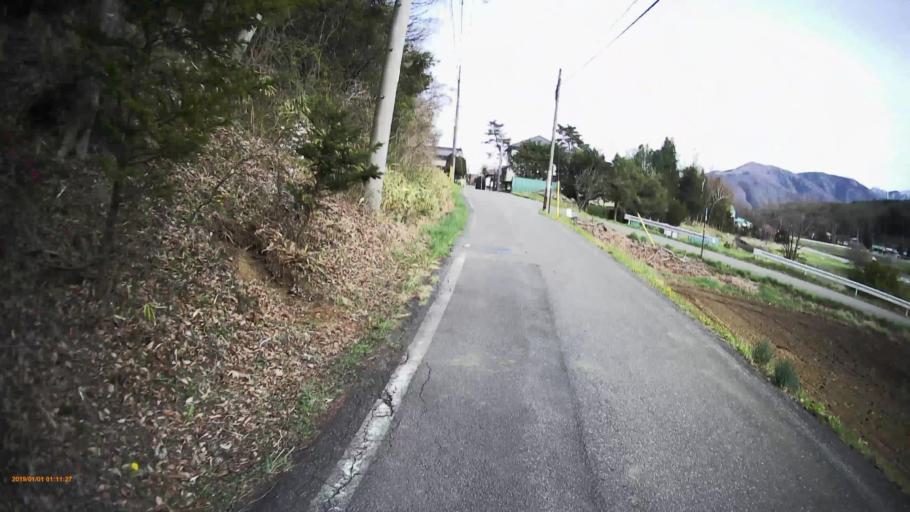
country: JP
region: Nagano
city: Chino
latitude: 35.9137
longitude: 138.2207
